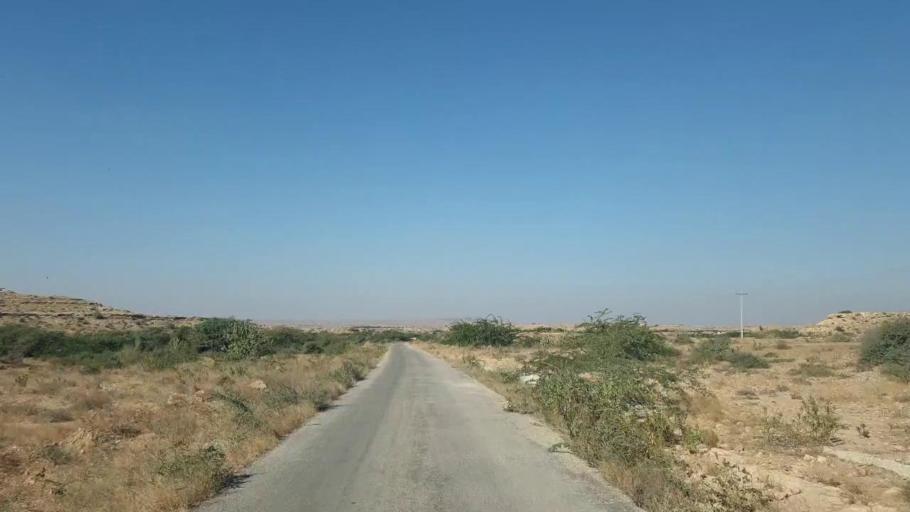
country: PK
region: Sindh
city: Gharo
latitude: 25.0836
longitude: 67.5367
